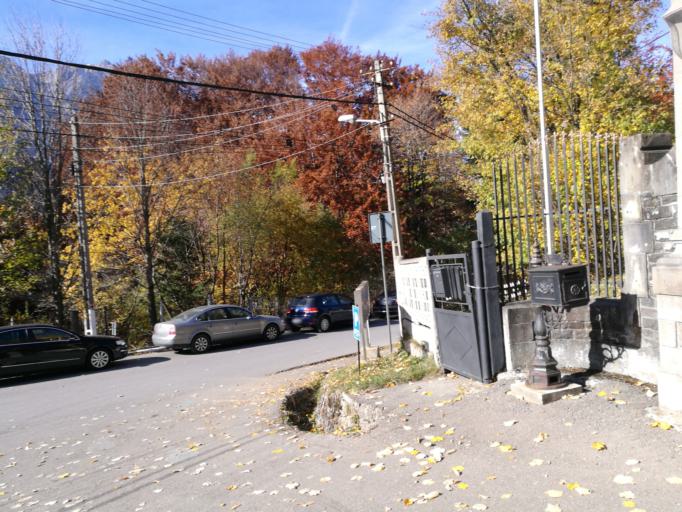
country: RO
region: Prahova
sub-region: Oras Busteni
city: Busteni
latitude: 45.4129
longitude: 25.5417
